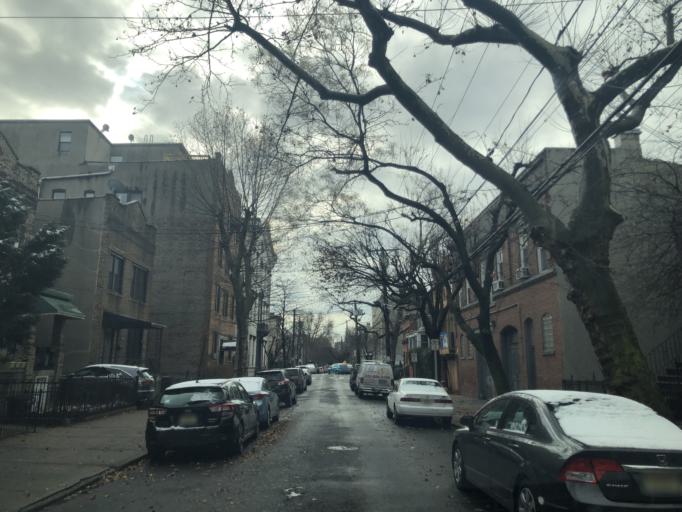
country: US
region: New Jersey
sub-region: Hudson County
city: Hoboken
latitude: 40.7403
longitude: -74.0456
